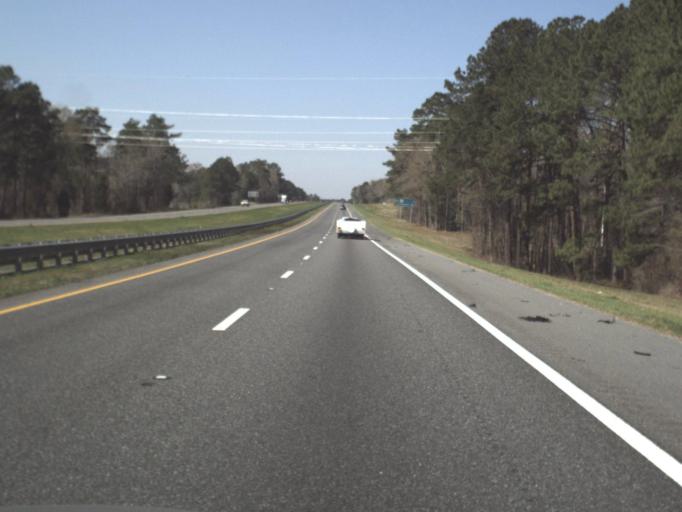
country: US
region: Florida
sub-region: Jackson County
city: Marianna
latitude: 30.7577
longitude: -85.2858
